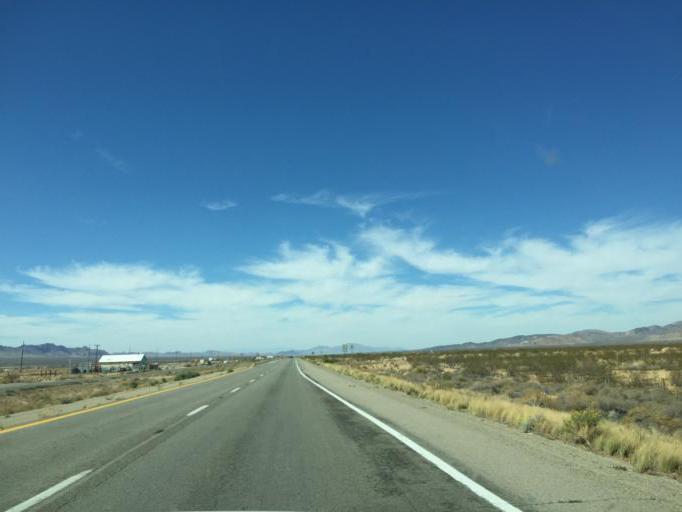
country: US
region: Arizona
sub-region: Mohave County
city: Dolan Springs
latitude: 35.5356
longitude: -114.3563
